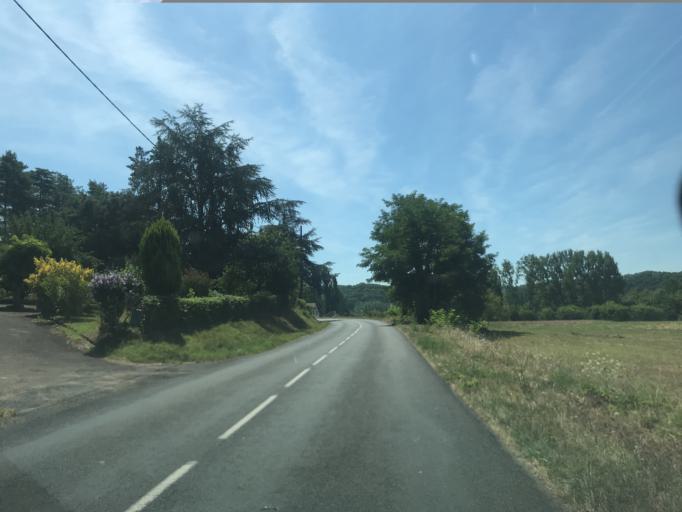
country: FR
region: Aquitaine
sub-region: Departement de la Dordogne
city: Cenac-et-Saint-Julien
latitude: 44.8109
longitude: 1.1972
